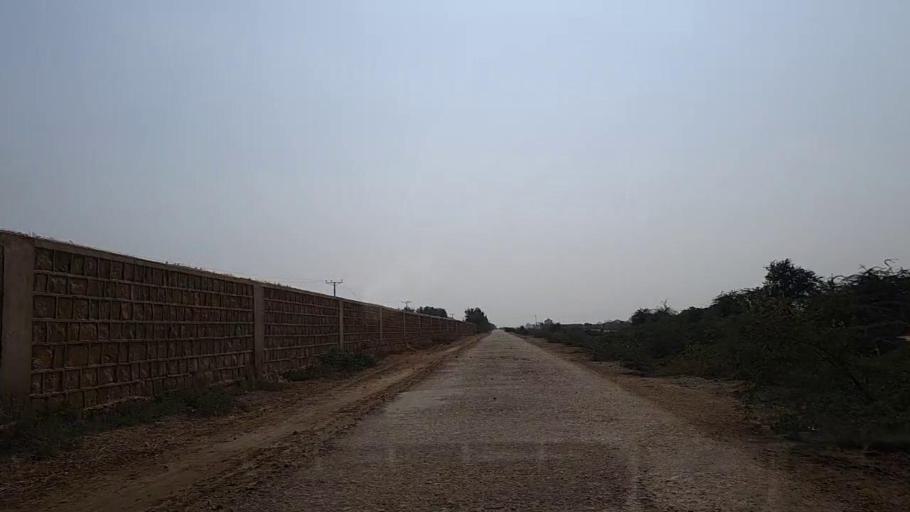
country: PK
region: Sindh
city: Thatta
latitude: 24.7246
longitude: 67.7684
